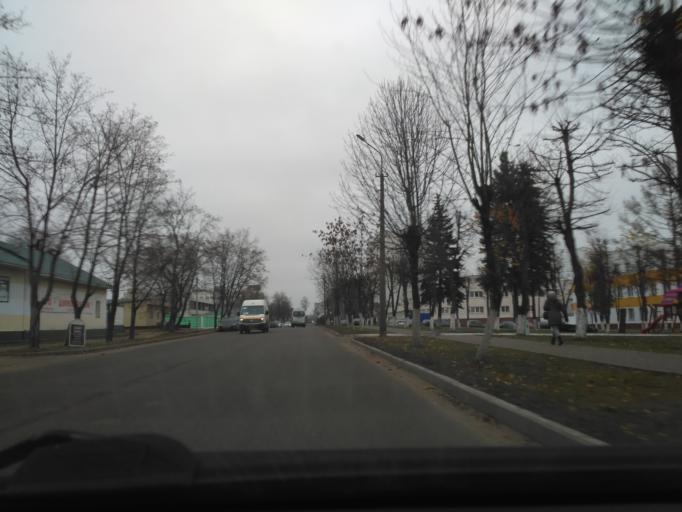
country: BY
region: Minsk
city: Horad Barysaw
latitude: 54.2108
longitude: 28.4902
